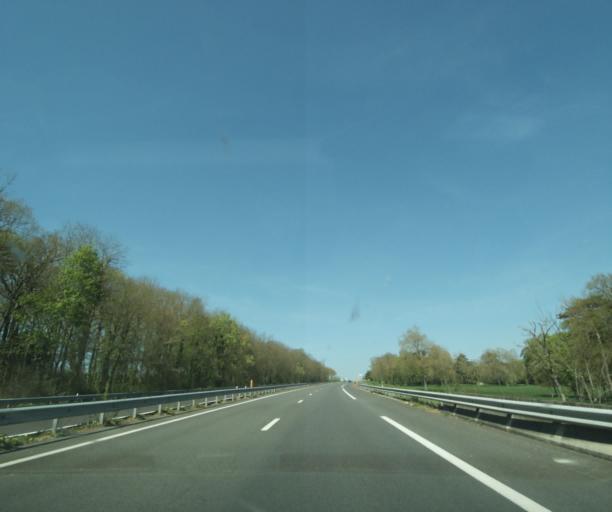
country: FR
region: Bourgogne
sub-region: Departement de la Nievre
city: Pouilly-sur-Loire
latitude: 47.2926
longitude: 2.9560
